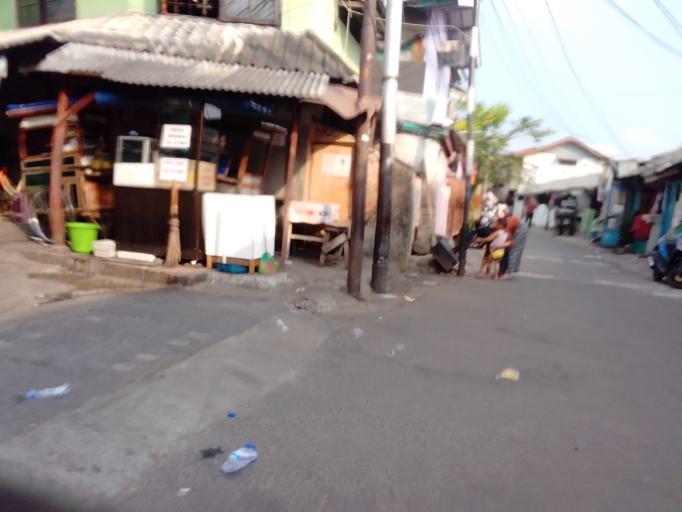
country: ID
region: Jakarta Raya
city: Jakarta
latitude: -6.1965
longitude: 106.8113
